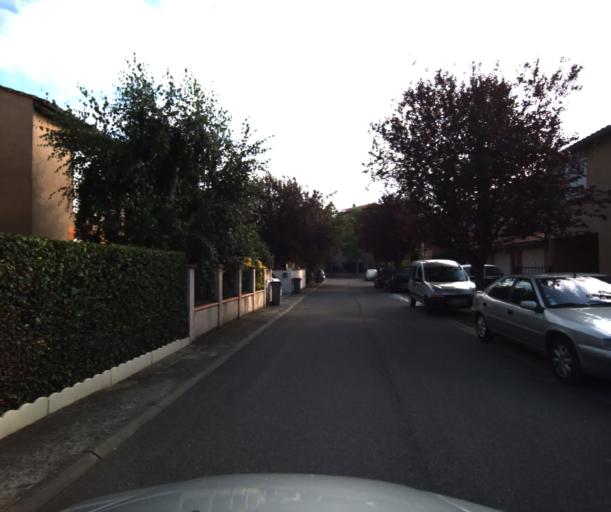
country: FR
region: Midi-Pyrenees
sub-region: Departement de la Haute-Garonne
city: Muret
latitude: 43.4575
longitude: 1.3316
